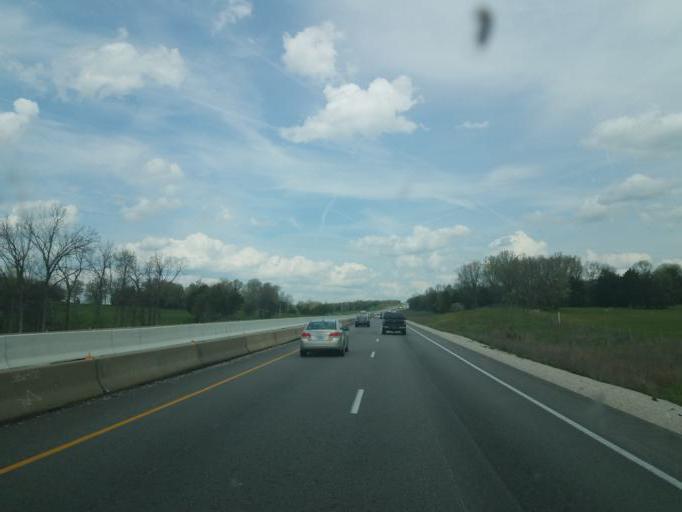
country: US
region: Kentucky
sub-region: Hart County
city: Munfordville
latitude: 37.4305
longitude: -85.8831
